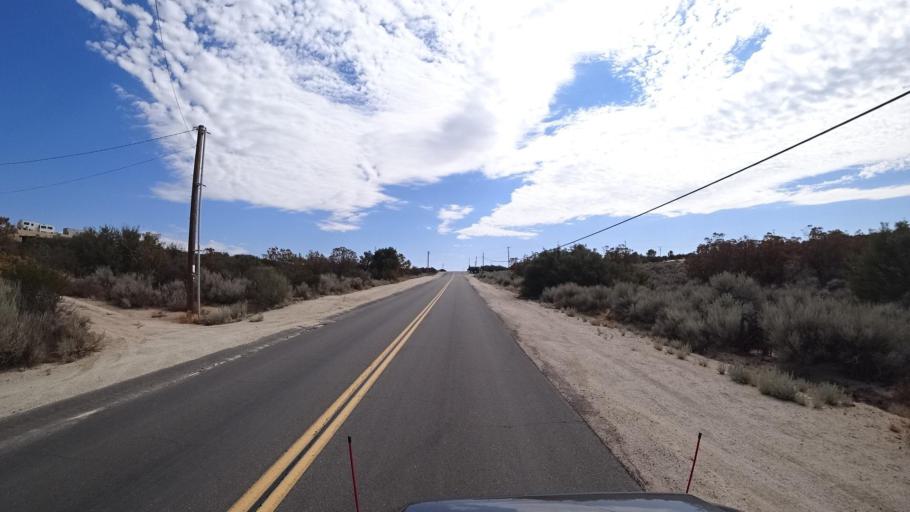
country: MX
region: Baja California
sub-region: Tecate
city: Cereso del Hongo
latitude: 32.6597
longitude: -116.2905
